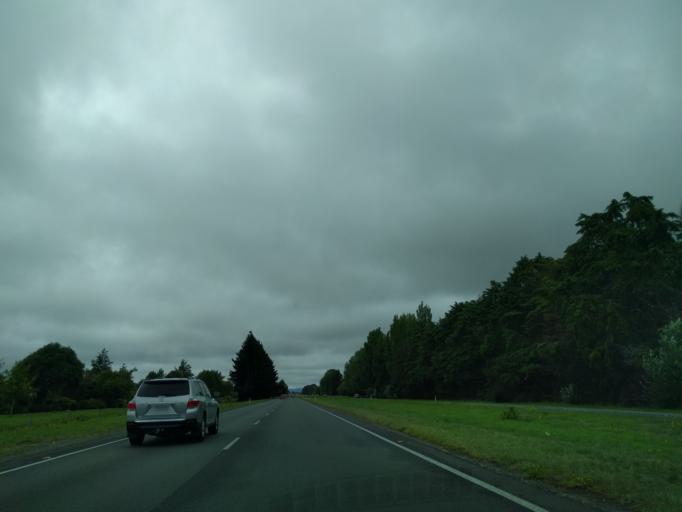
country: NZ
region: Canterbury
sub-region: Waimakariri District
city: Kaiapoi
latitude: -43.3933
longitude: 172.6404
